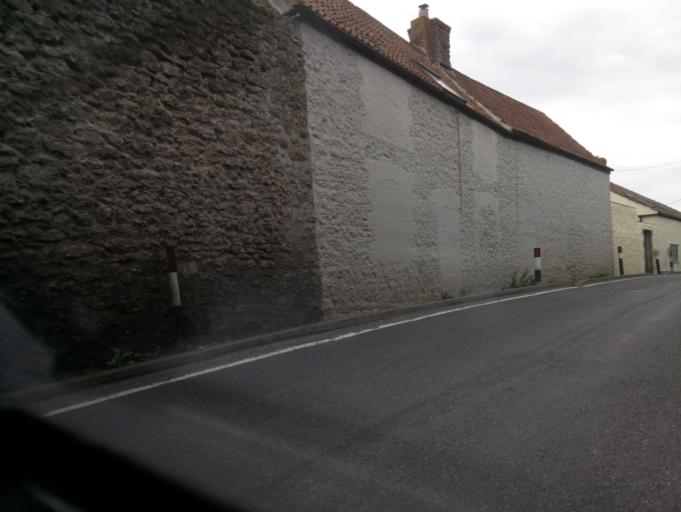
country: GB
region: England
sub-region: Somerset
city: Wells
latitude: 51.2323
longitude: -2.7076
